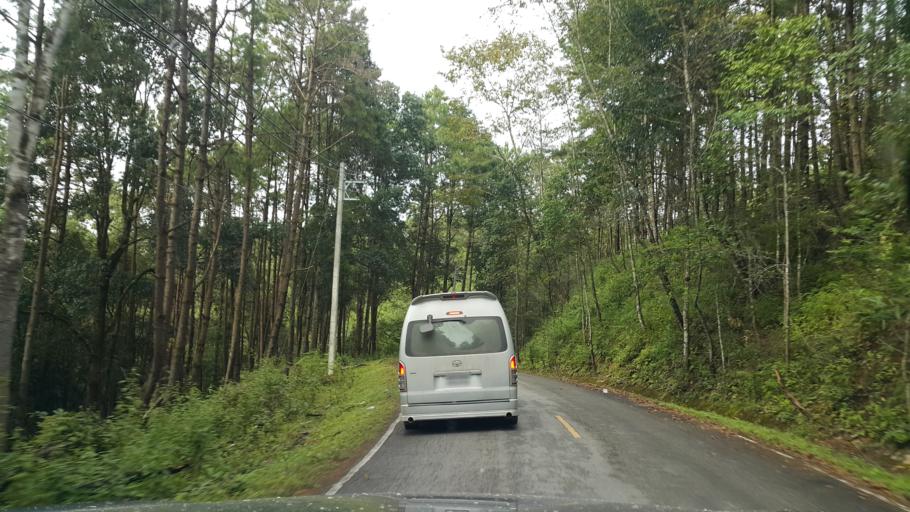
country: TH
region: Chiang Mai
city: Chaem Luang
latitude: 18.9259
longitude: 98.4775
